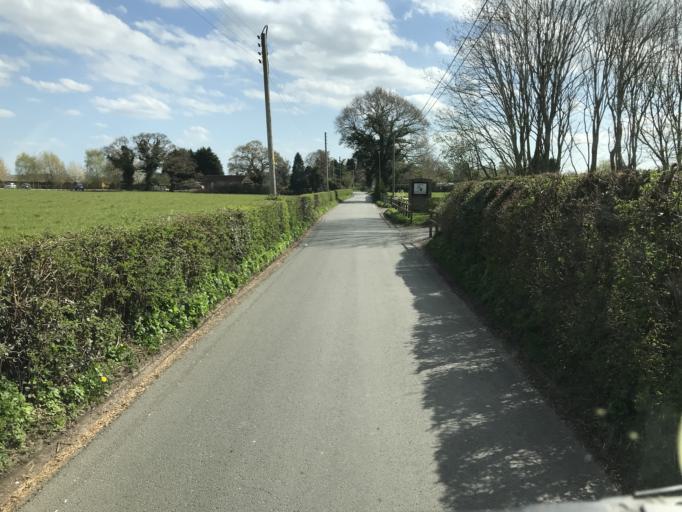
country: GB
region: England
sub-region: Cheshire West and Chester
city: Tarvin
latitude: 53.2094
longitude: -2.7681
